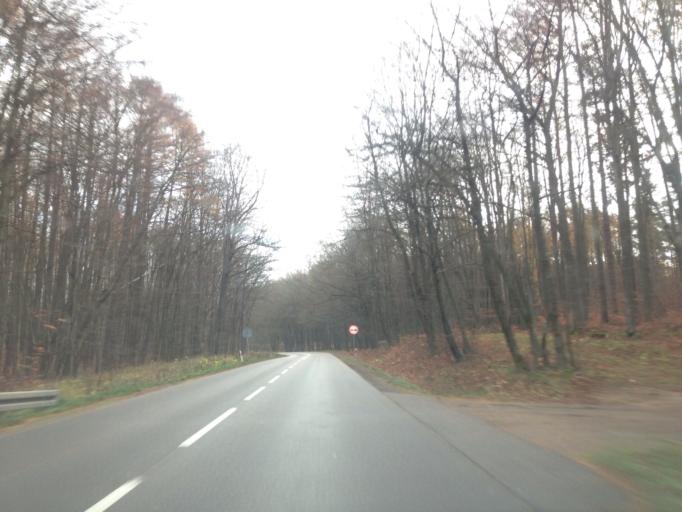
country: PL
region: Pomeranian Voivodeship
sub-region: Powiat gdanski
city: Kolbudy
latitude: 54.2529
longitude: 18.4031
